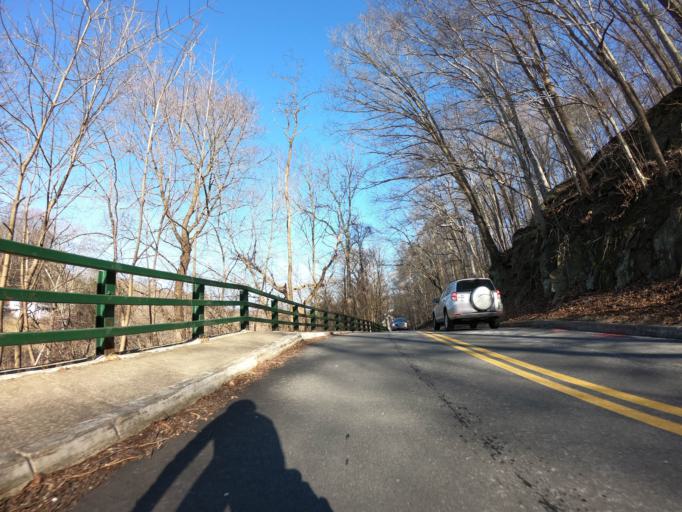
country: US
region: Maryland
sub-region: Howard County
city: Ellicott City
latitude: 39.2707
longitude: -76.7930
